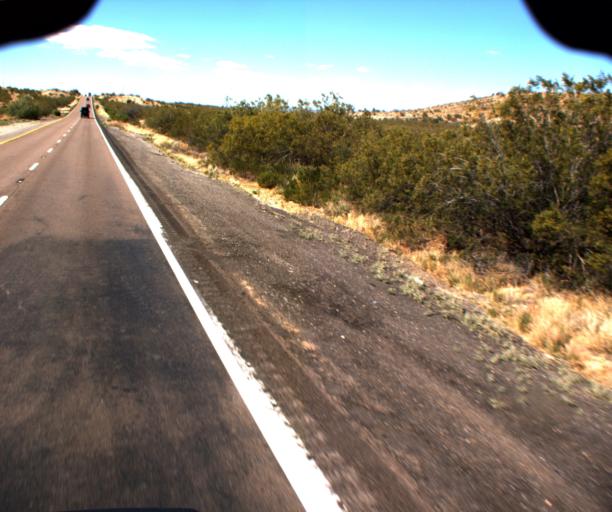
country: US
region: Arizona
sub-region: Mohave County
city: Kingman
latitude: 35.0214
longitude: -113.6641
